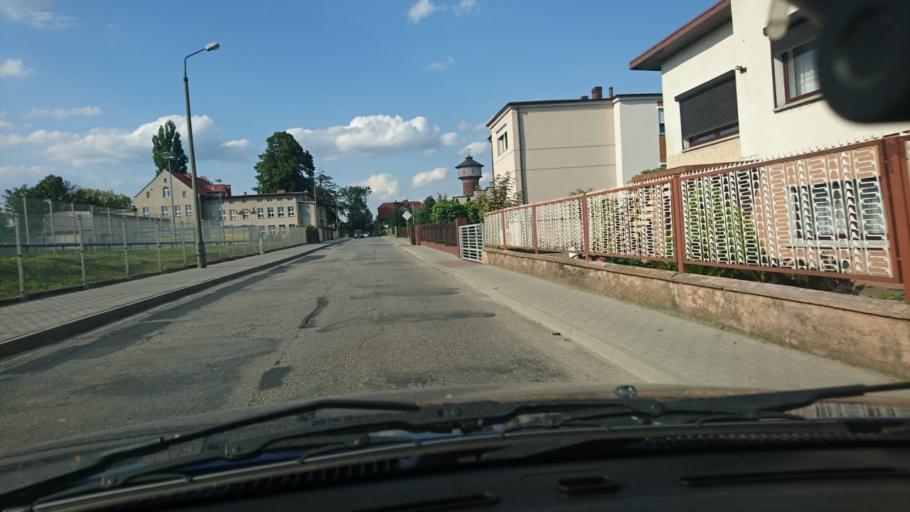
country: PL
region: Greater Poland Voivodeship
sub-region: Powiat ostrowski
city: Odolanow
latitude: 51.5795
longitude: 17.6605
